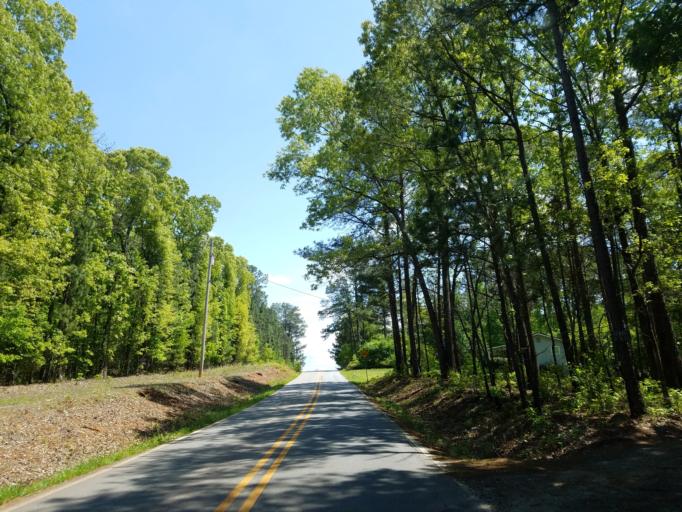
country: US
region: Georgia
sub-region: Butts County
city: Indian Springs
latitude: 33.1680
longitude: -84.0194
